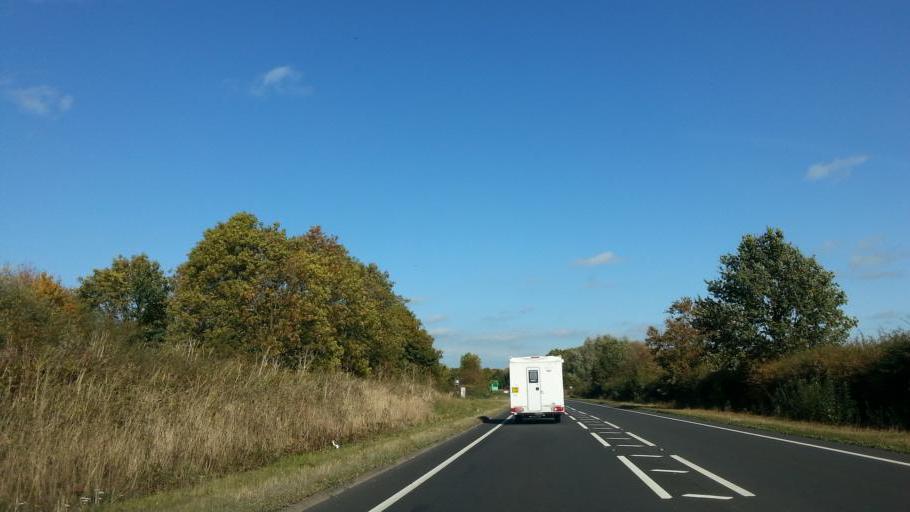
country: GB
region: England
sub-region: Northamptonshire
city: Oundle
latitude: 52.4484
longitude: -0.4646
